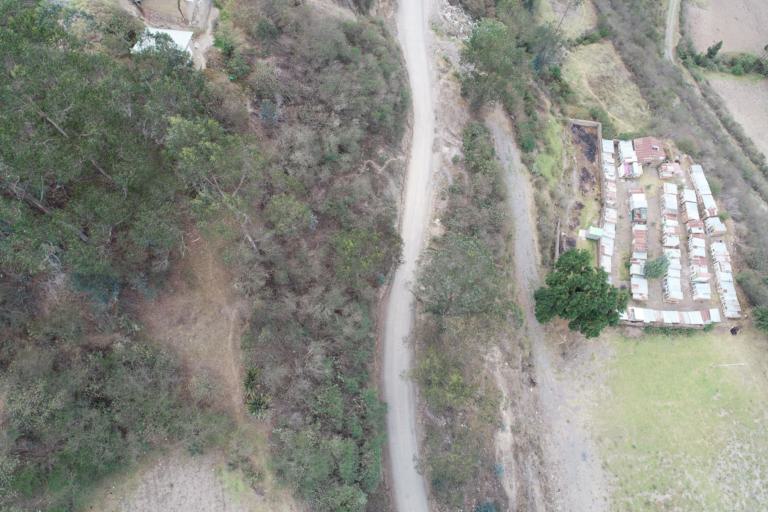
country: BO
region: La Paz
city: Sorata
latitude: -15.6385
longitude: -68.7032
